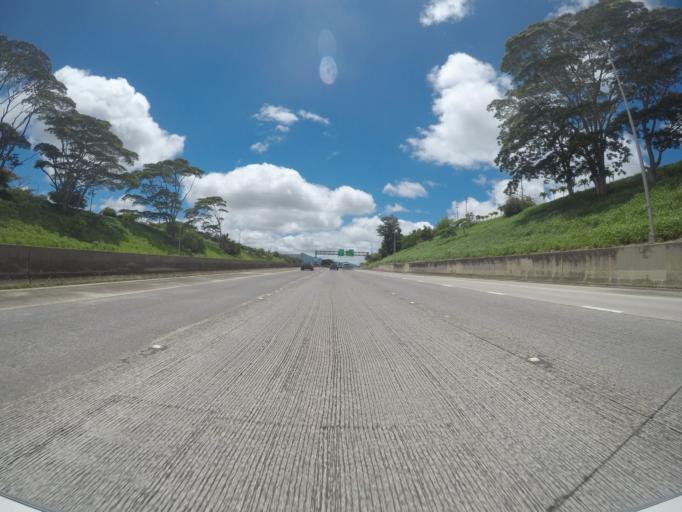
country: US
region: Hawaii
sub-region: Honolulu County
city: Mililani Town
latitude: 21.4623
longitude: -157.9979
